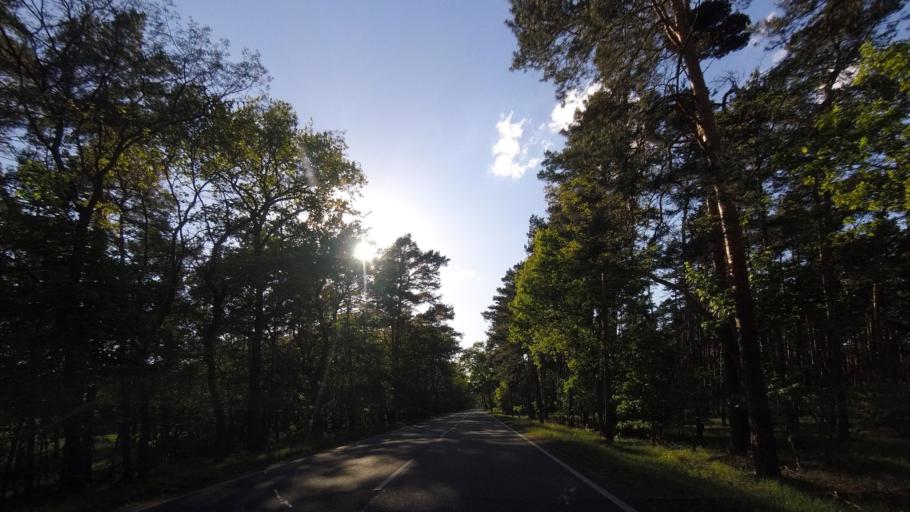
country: DE
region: Brandenburg
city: Kasel-Golzig
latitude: 51.9659
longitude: 13.7042
